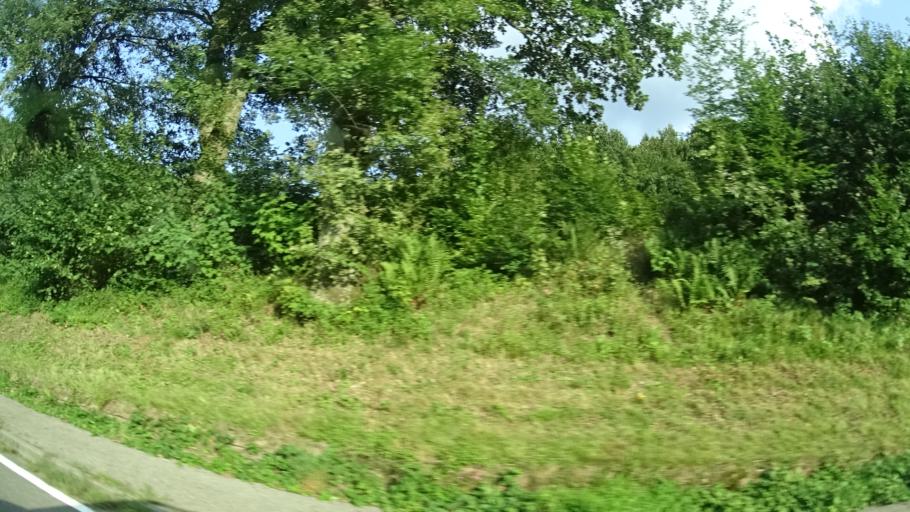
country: DE
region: Baden-Wuerttemberg
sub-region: Karlsruhe Region
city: Heddesbach
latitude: 49.5196
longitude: 8.8620
